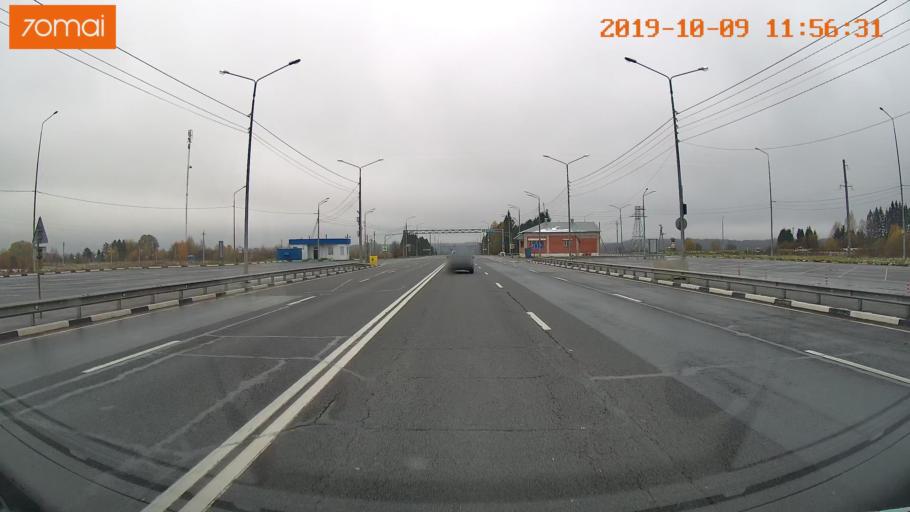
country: RU
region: Vologda
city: Gryazovets
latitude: 58.7432
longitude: 40.2880
